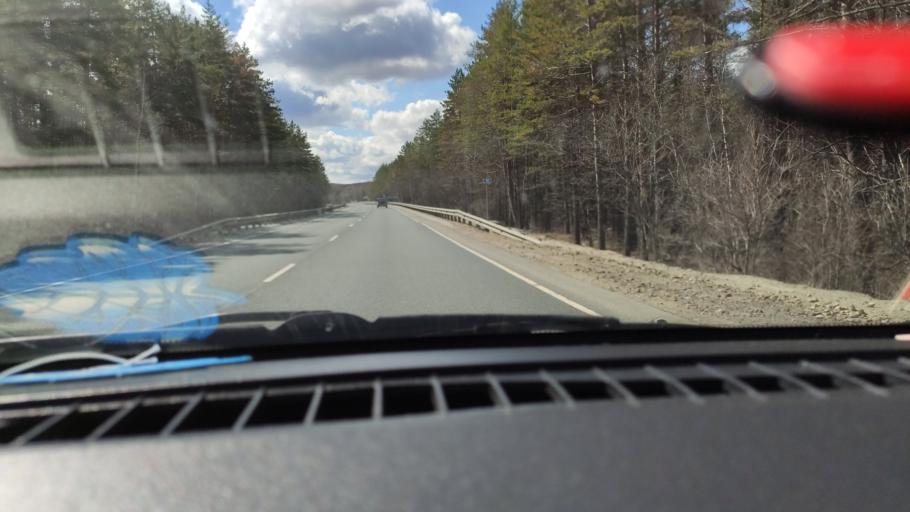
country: RU
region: Saratov
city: Khvalynsk
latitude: 52.5148
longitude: 48.0168
